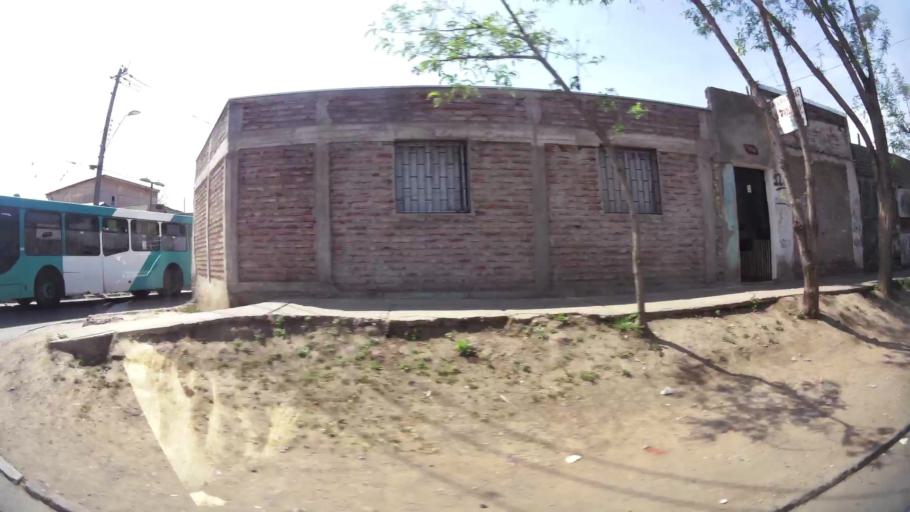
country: CL
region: Santiago Metropolitan
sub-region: Provincia de Santiago
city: Lo Prado
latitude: -33.4322
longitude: -70.7303
